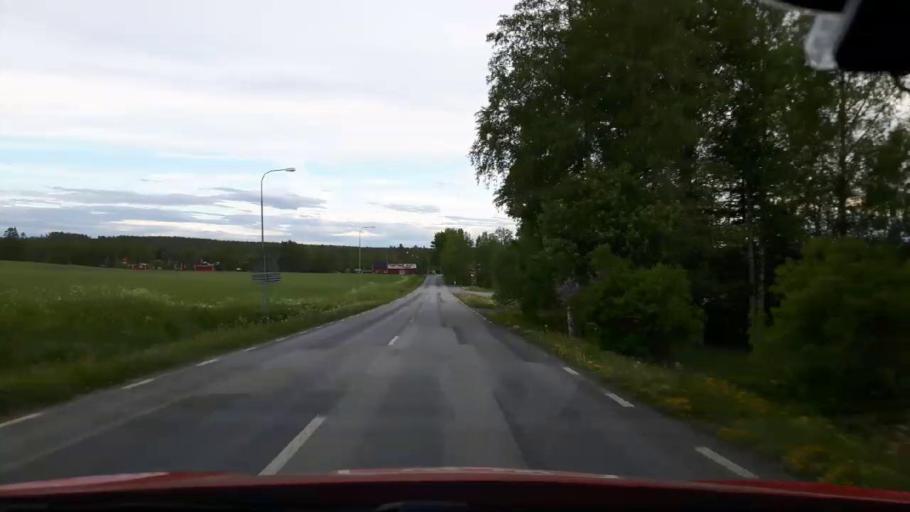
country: SE
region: Jaemtland
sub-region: OEstersunds Kommun
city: Ostersund
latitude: 63.1316
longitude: 14.4539
